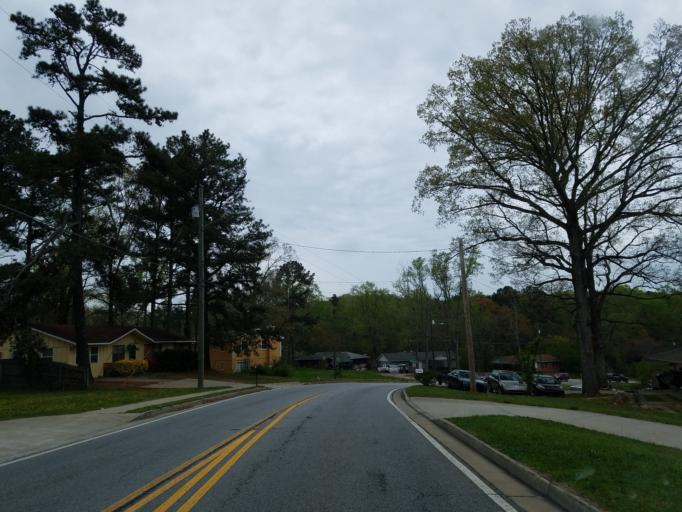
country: US
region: Georgia
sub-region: Cobb County
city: Fair Oaks
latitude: 33.8890
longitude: -84.5509
